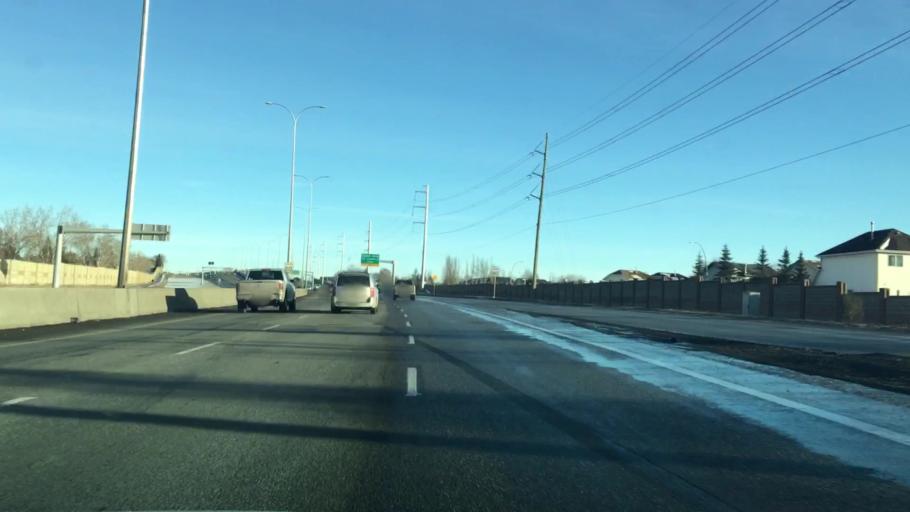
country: CA
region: Alberta
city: Calgary
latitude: 50.9795
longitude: -114.0113
